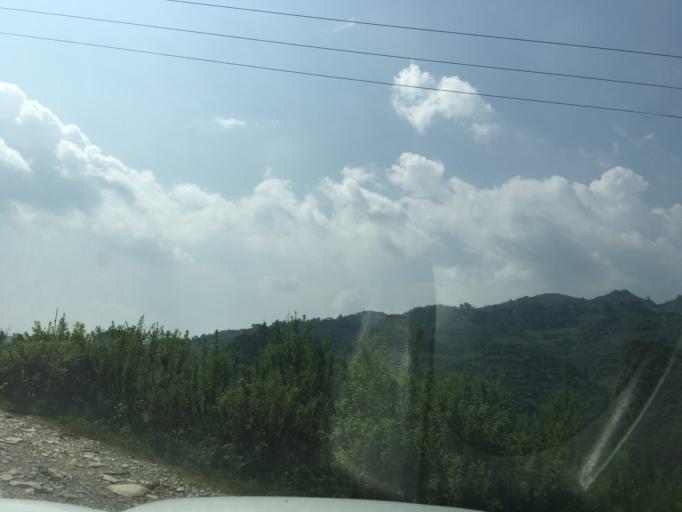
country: CN
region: Guangxi Zhuangzu Zizhiqu
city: Xinzhou
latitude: 24.9910
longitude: 105.7402
